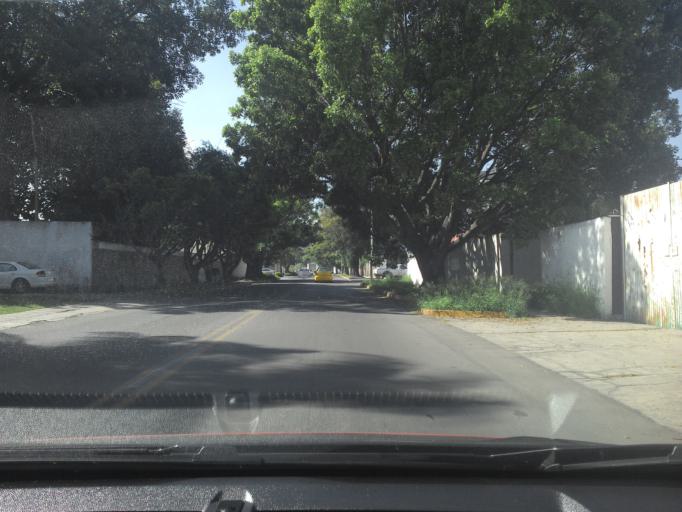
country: MX
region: Jalisco
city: Zapopan2
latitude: 20.6937
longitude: -103.4038
